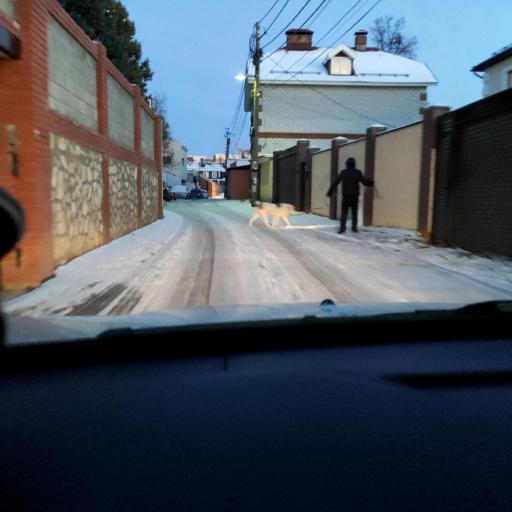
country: RU
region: Samara
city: Samara
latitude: 53.2601
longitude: 50.1957
